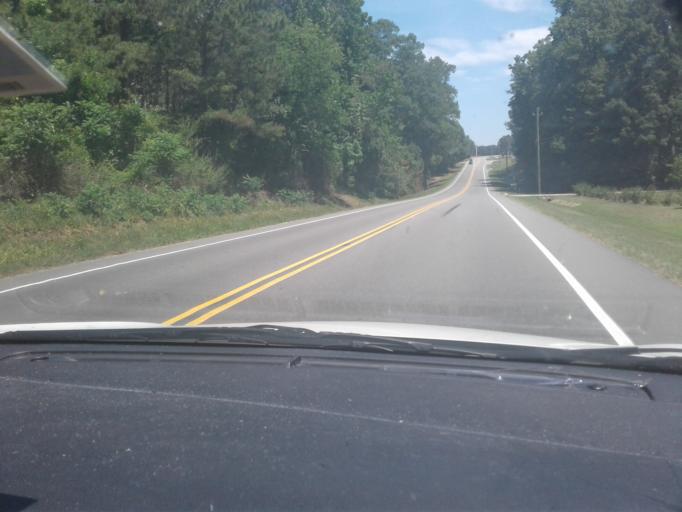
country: US
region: North Carolina
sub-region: Harnett County
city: Lillington
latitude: 35.4690
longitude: -78.8277
